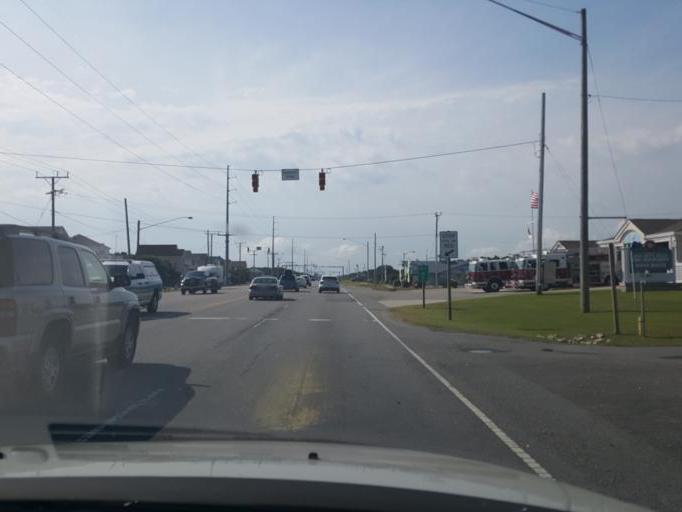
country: US
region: North Carolina
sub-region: Dare County
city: Kill Devil Hills
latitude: 36.0308
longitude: -75.6713
